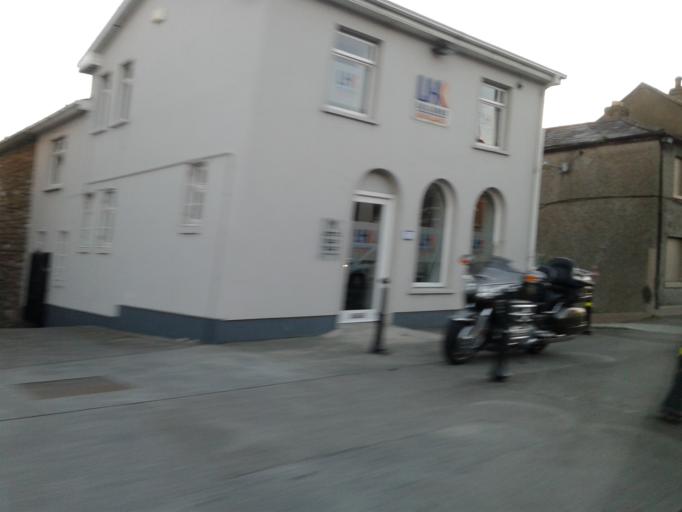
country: IE
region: Leinster
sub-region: Lu
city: Drogheda
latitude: 53.7165
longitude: -6.3585
